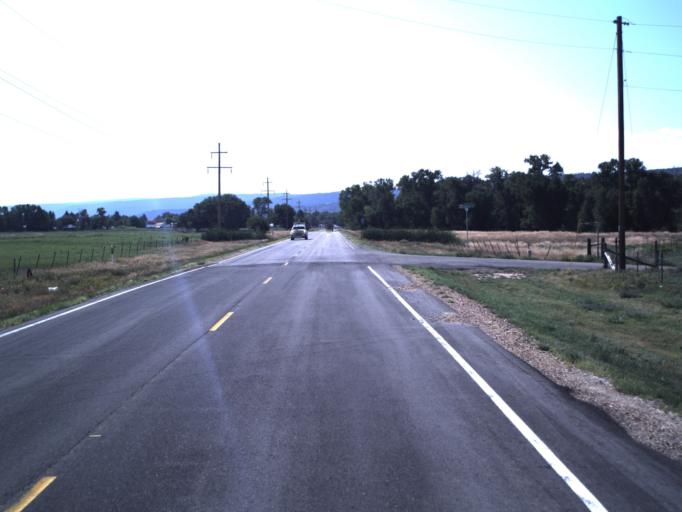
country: US
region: Utah
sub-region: Duchesne County
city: Duchesne
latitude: 40.3605
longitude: -110.7184
